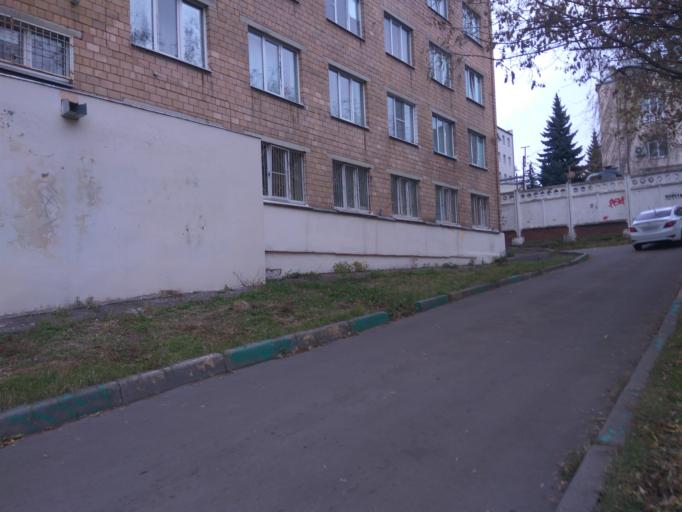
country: RU
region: Moscow
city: Kolomenskoye
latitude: 55.6417
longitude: 37.6733
